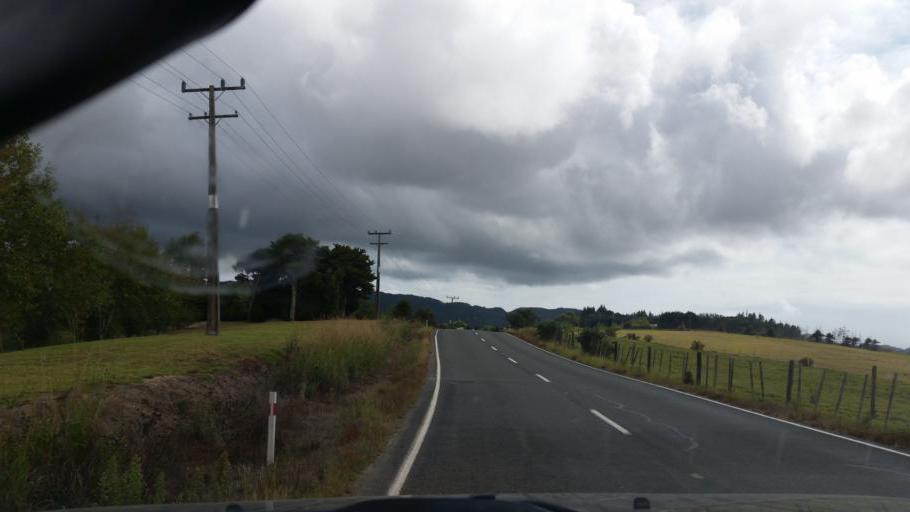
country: NZ
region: Auckland
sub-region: Auckland
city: Wellsford
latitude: -36.1089
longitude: 174.5529
